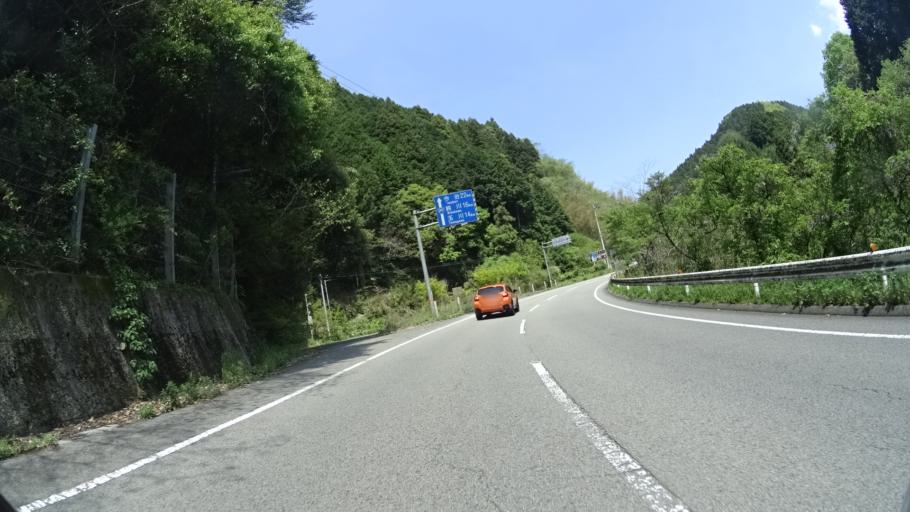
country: JP
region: Ehime
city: Hojo
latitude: 33.9229
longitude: 132.8865
